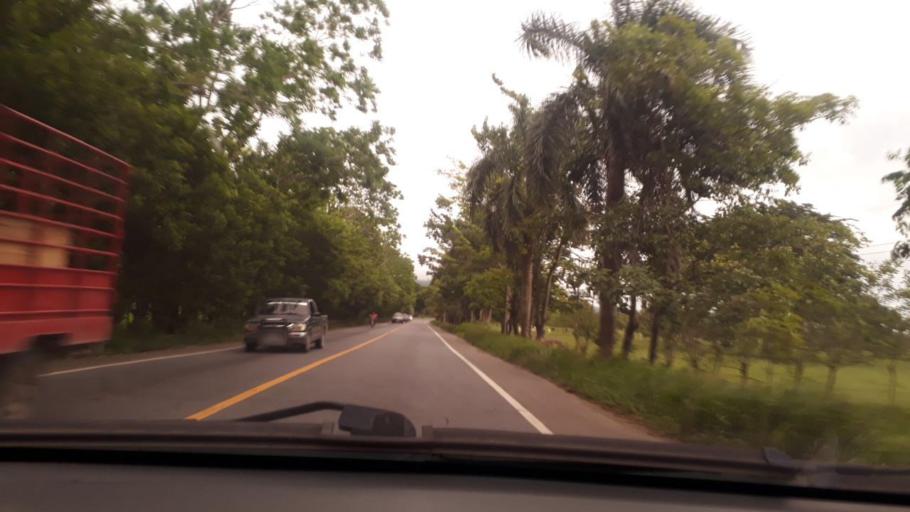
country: GT
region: Izabal
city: Morales
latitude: 15.4657
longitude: -88.9093
